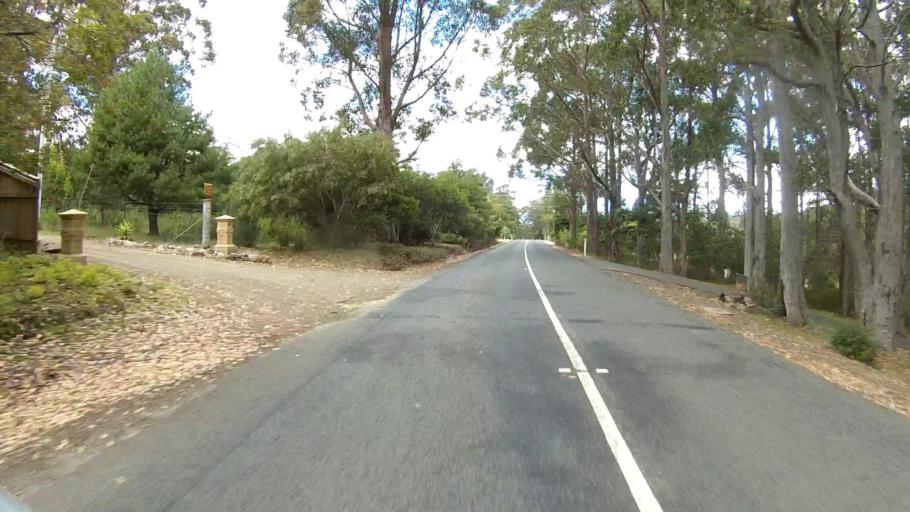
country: AU
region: Tasmania
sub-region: Kingborough
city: Margate
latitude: -42.9729
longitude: 147.1679
